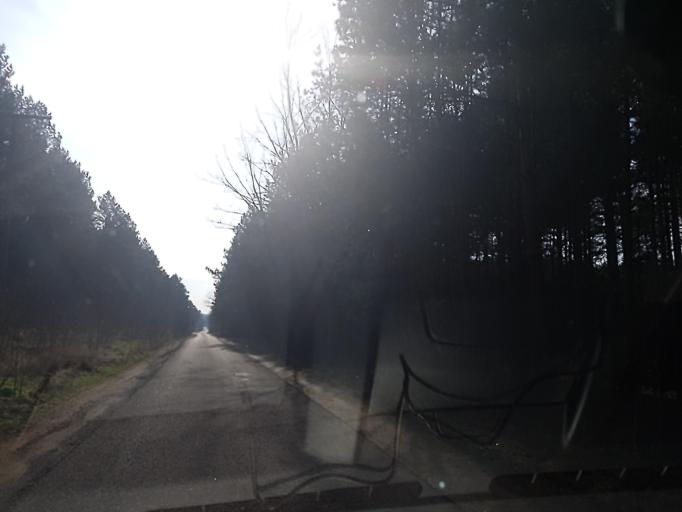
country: DE
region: Brandenburg
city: Wenzlow
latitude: 52.3328
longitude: 12.4395
